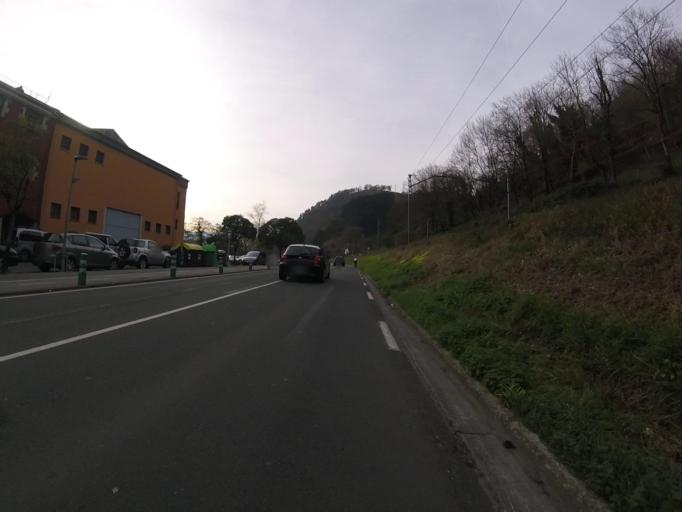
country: ES
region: Basque Country
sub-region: Provincia de Guipuzcoa
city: Anoeta
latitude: 43.1521
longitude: -2.0716
